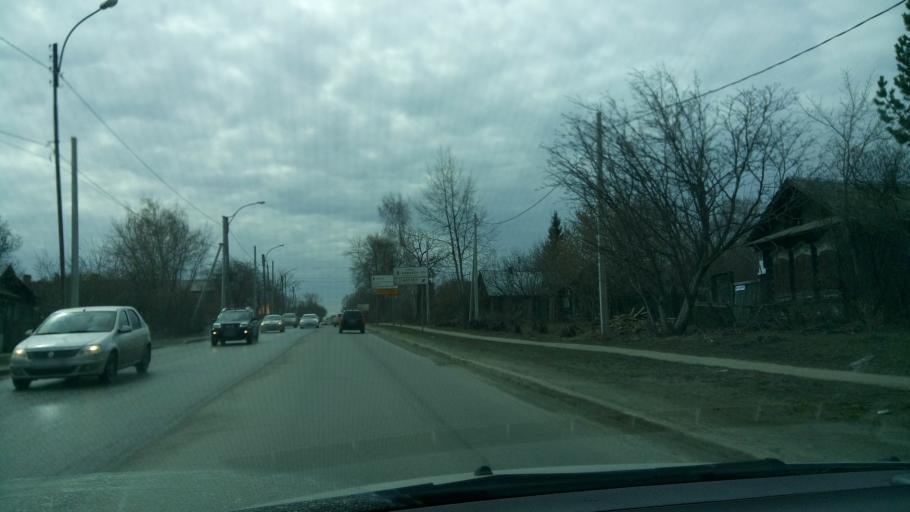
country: RU
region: Sverdlovsk
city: Yekaterinburg
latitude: 56.8708
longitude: 60.6821
